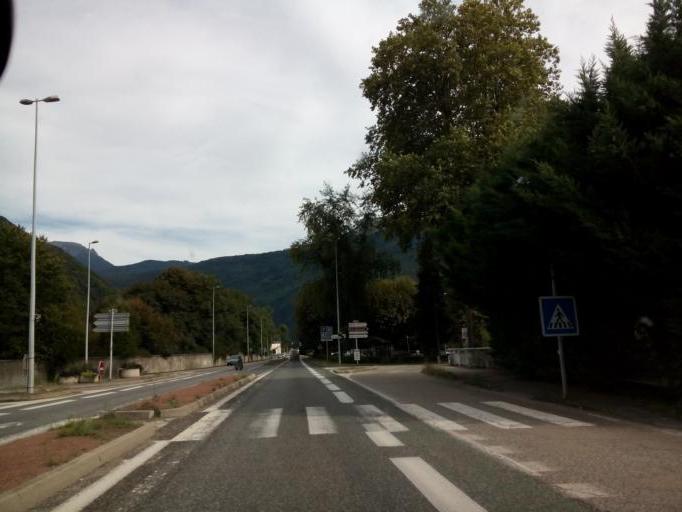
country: FR
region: Rhone-Alpes
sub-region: Departement de l'Isere
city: Notre-Dame-de-Mesage
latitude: 45.0596
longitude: 5.7674
